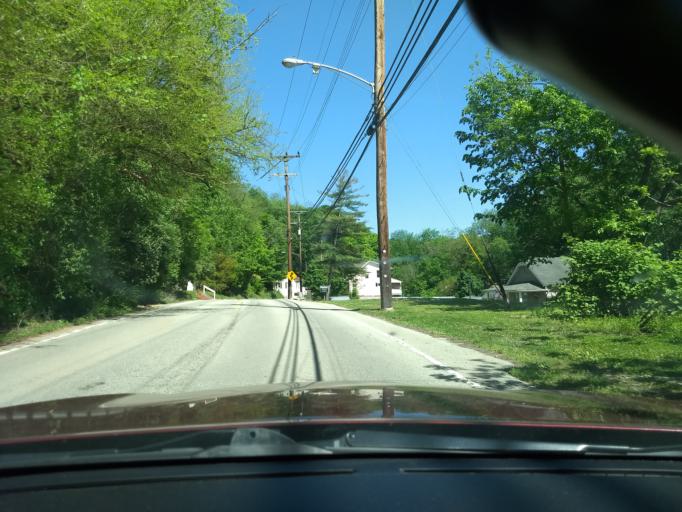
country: US
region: Pennsylvania
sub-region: Allegheny County
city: Heidelberg
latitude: 40.3928
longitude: -80.0798
